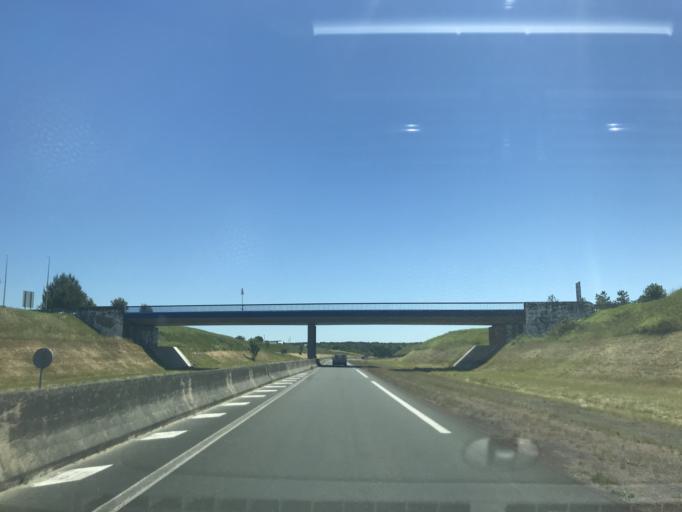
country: FR
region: Poitou-Charentes
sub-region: Departement de la Charente-Maritime
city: Saint-Georges-de-Didonne
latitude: 45.6059
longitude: -0.9747
